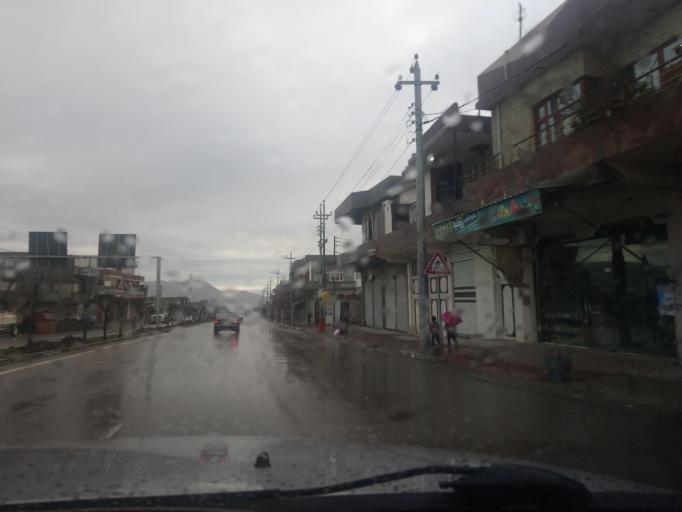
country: IQ
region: As Sulaymaniyah
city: Qeladize
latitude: 36.1779
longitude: 45.1544
